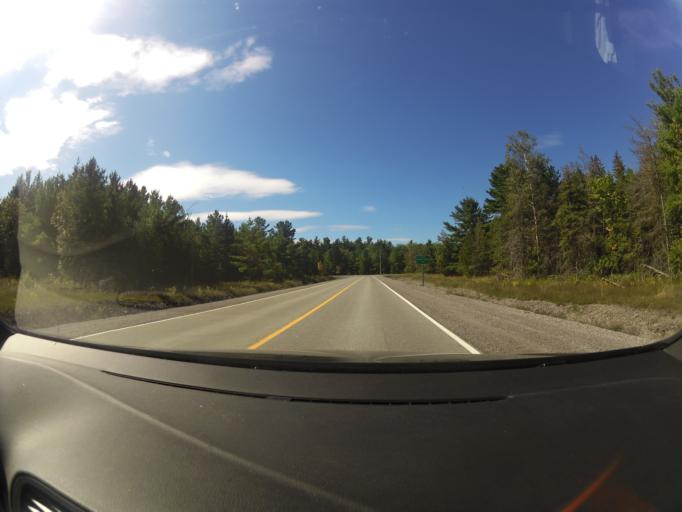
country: CA
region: Ontario
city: Bells Corners
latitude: 45.2485
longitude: -75.9837
